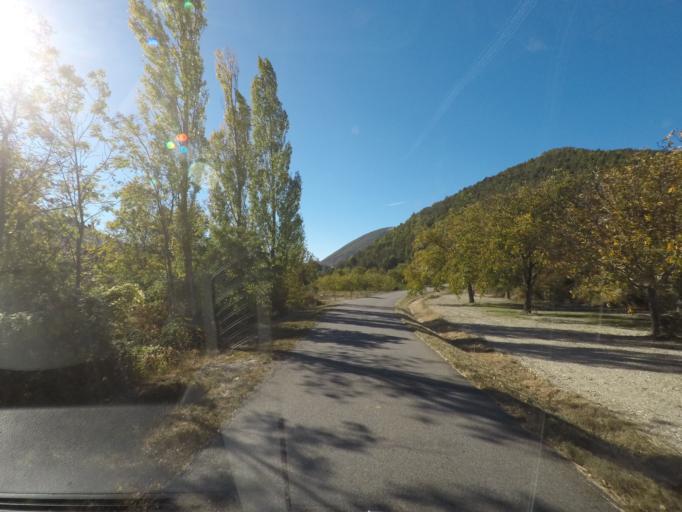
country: FR
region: Provence-Alpes-Cote d'Azur
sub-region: Departement des Hautes-Alpes
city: Serres
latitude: 44.4691
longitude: 5.4730
